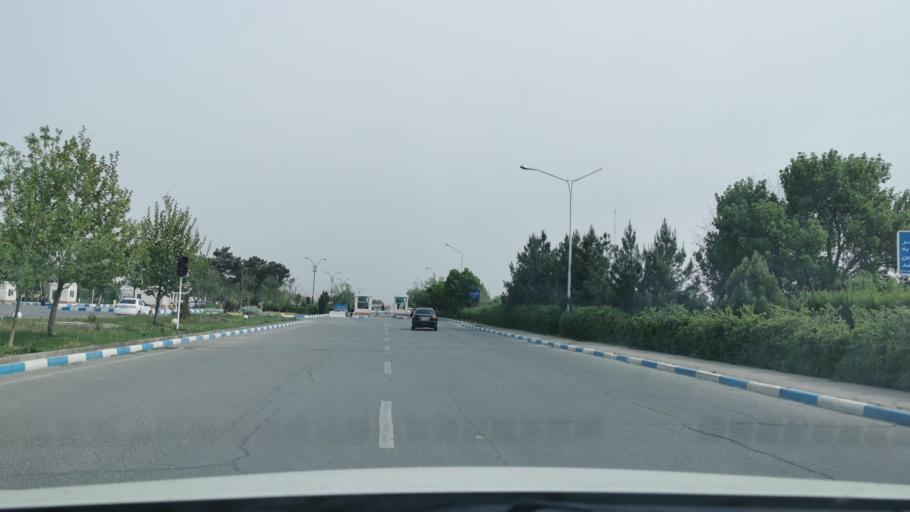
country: IR
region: Razavi Khorasan
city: Mashhad
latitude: 36.2303
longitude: 59.6367
